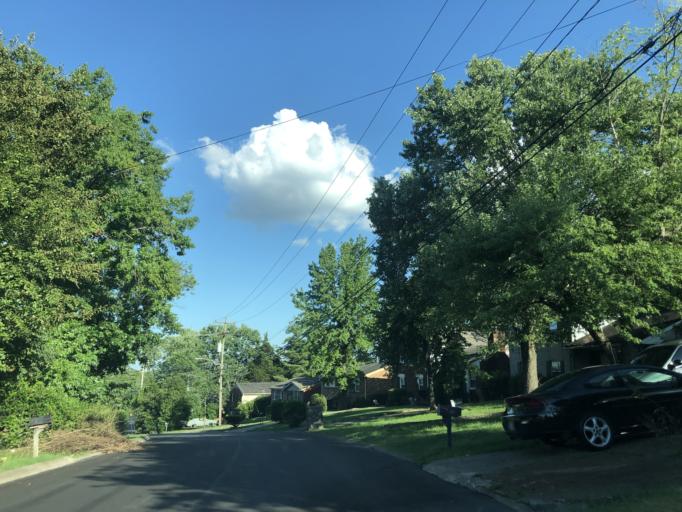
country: US
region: Tennessee
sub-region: Davidson County
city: Nashville
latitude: 36.1851
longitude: -86.8445
